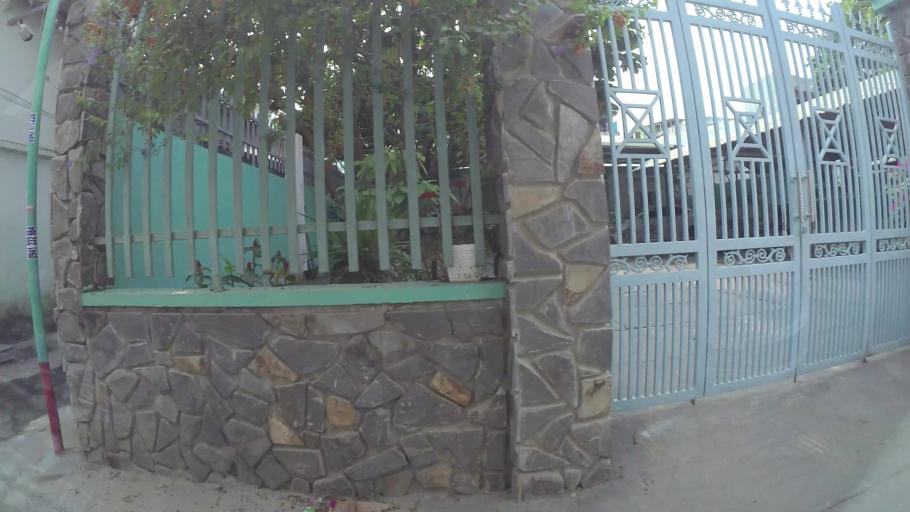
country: VN
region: Da Nang
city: Son Tra
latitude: 16.0428
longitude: 108.2172
